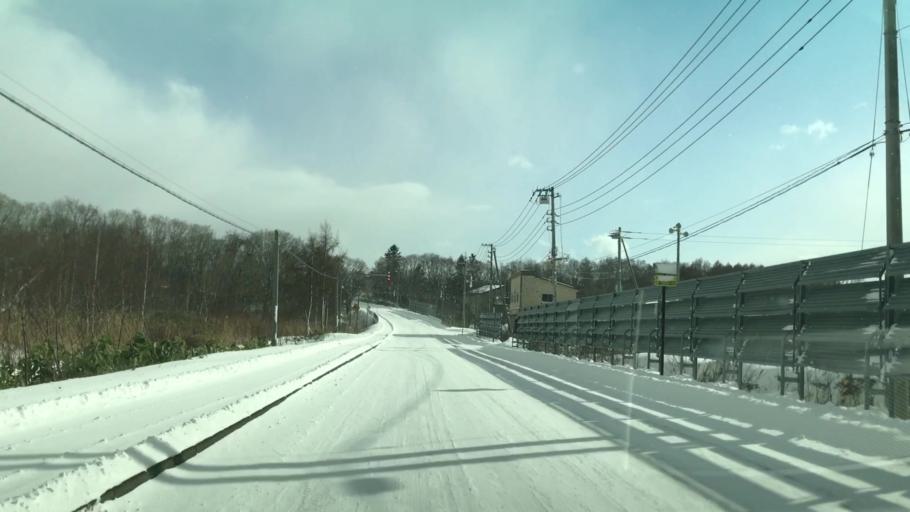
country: JP
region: Hokkaido
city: Yoichi
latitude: 43.3064
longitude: 140.5559
